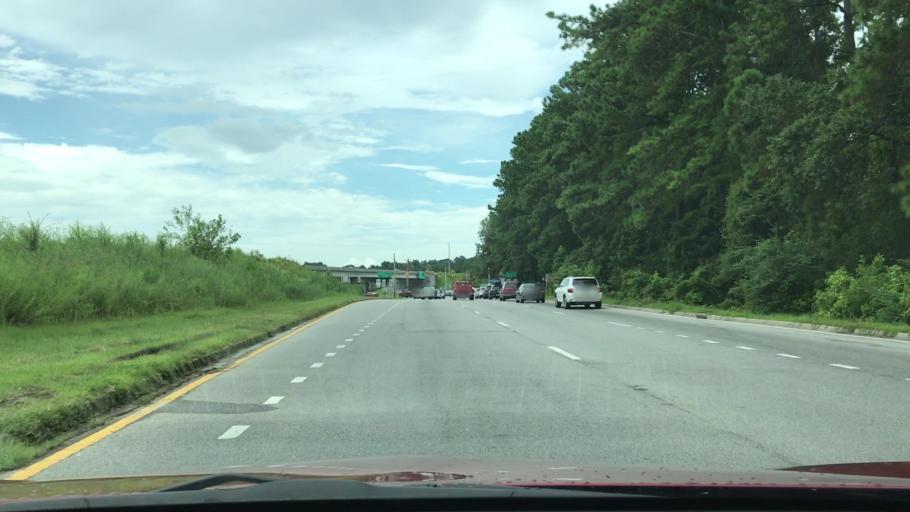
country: US
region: South Carolina
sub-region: Charleston County
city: Shell Point
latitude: 32.7931
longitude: -80.0334
